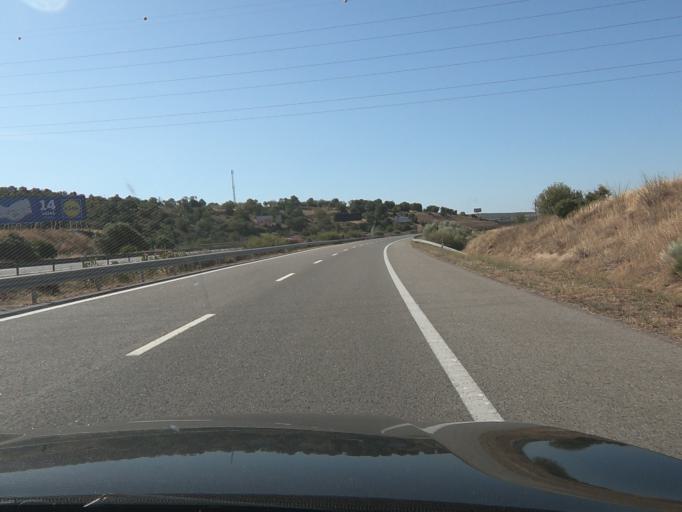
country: PT
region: Faro
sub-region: Albufeira
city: Ferreiras
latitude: 37.1852
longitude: -8.2179
